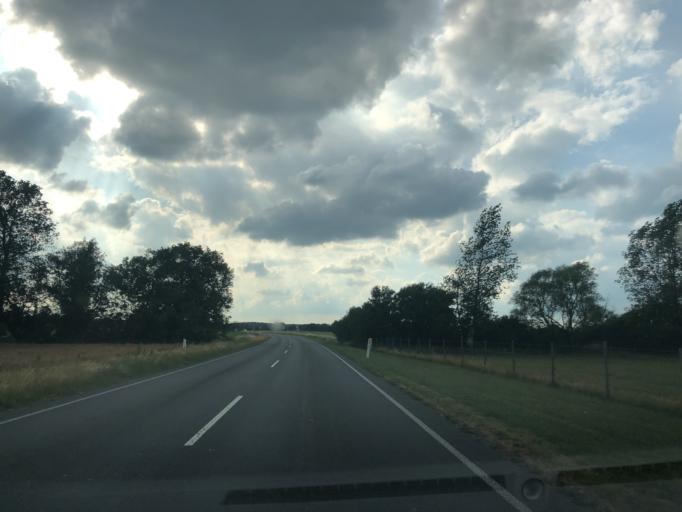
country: DK
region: Zealand
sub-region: Stevns Kommune
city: Harlev
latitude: 55.3146
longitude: 12.2144
